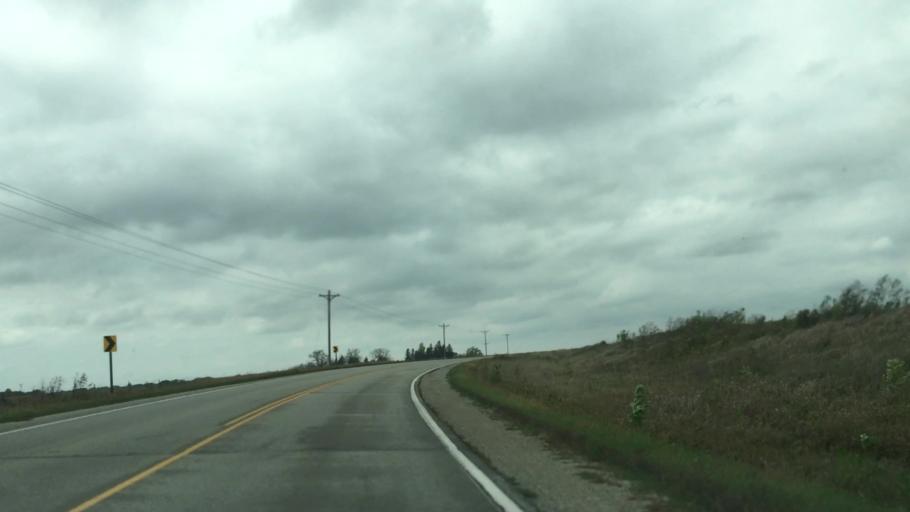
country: US
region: Minnesota
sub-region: Fillmore County
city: Preston
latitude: 43.7324
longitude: -92.0947
